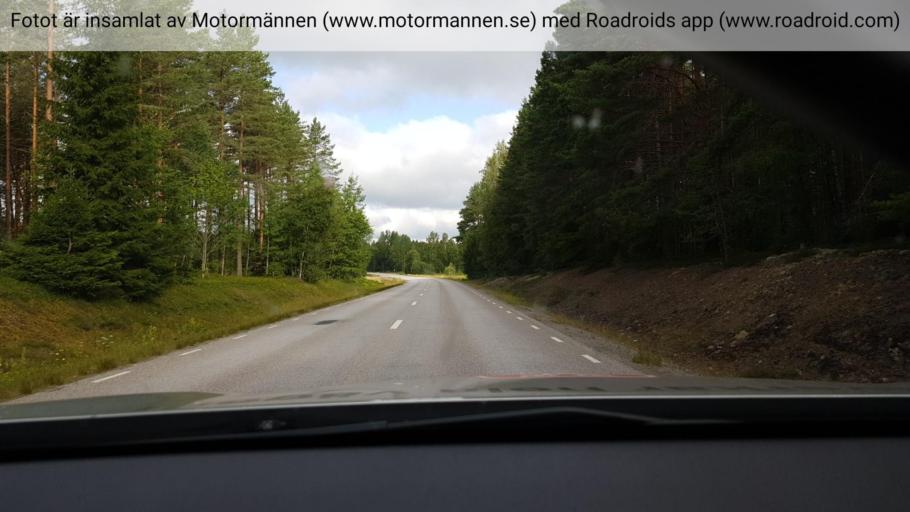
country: SE
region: Stockholm
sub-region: Norrtalje Kommun
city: Nykvarn
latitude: 59.9025
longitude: 18.3376
